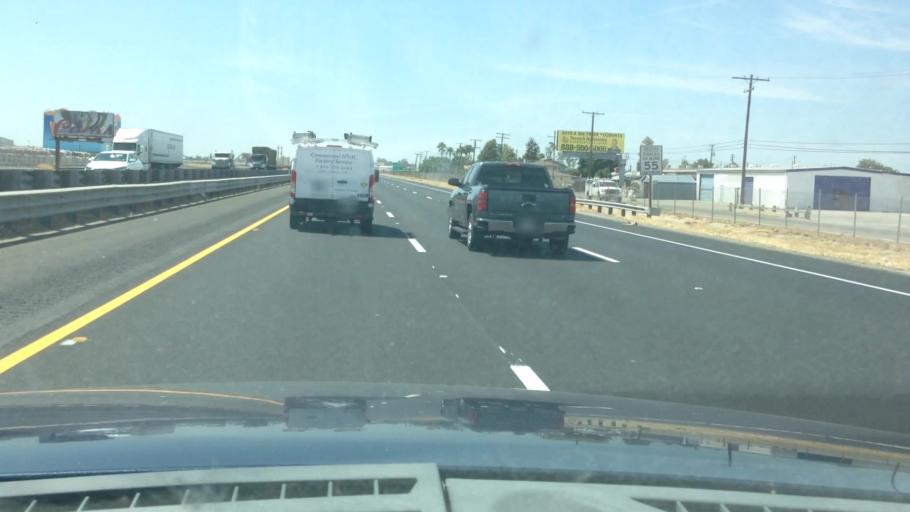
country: US
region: California
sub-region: Kern County
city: Delano
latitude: 35.7388
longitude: -119.2413
